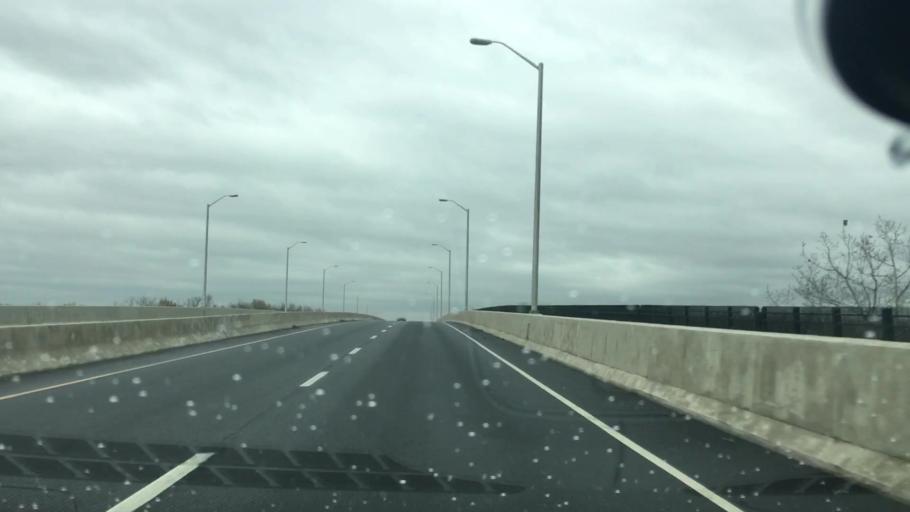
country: US
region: Connecticut
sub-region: Hartford County
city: Wethersfield
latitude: 41.7132
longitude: -72.6417
